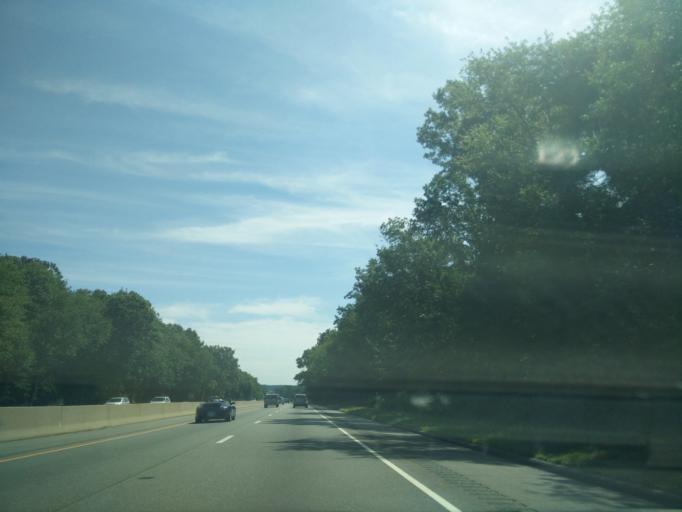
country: US
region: Connecticut
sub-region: New Haven County
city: Guilford Center
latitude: 41.2890
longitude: -72.6555
